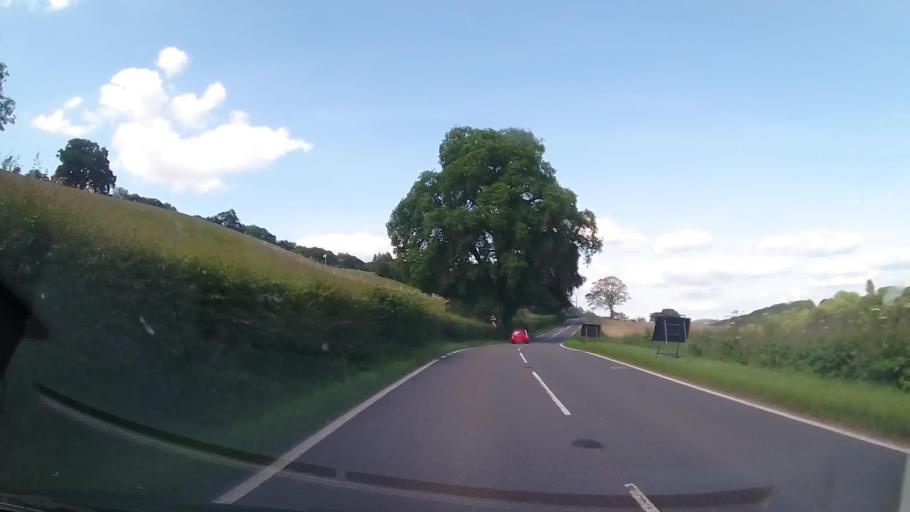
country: GB
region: Wales
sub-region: Sir Powys
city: Llanfyllin
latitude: 52.6555
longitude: -3.3196
